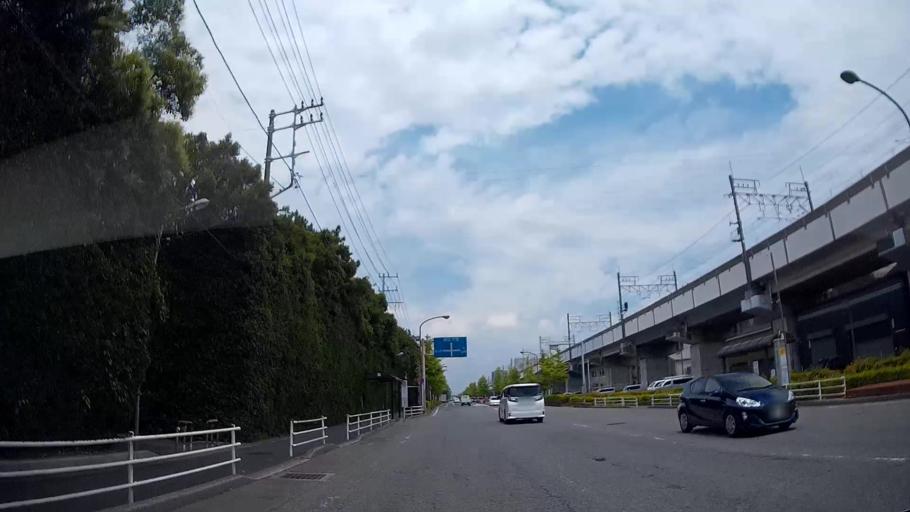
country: JP
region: Tokyo
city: Urayasu
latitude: 35.6397
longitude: 139.9002
